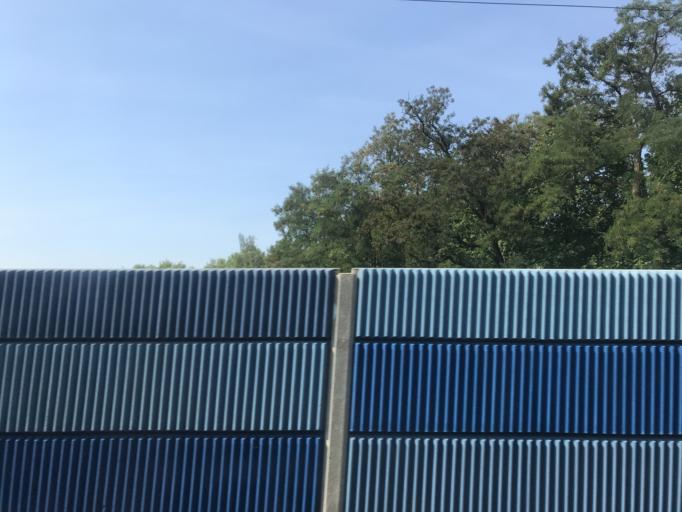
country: CZ
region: Central Bohemia
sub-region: Okres Benesov
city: Cercany
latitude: 49.8553
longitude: 14.6982
